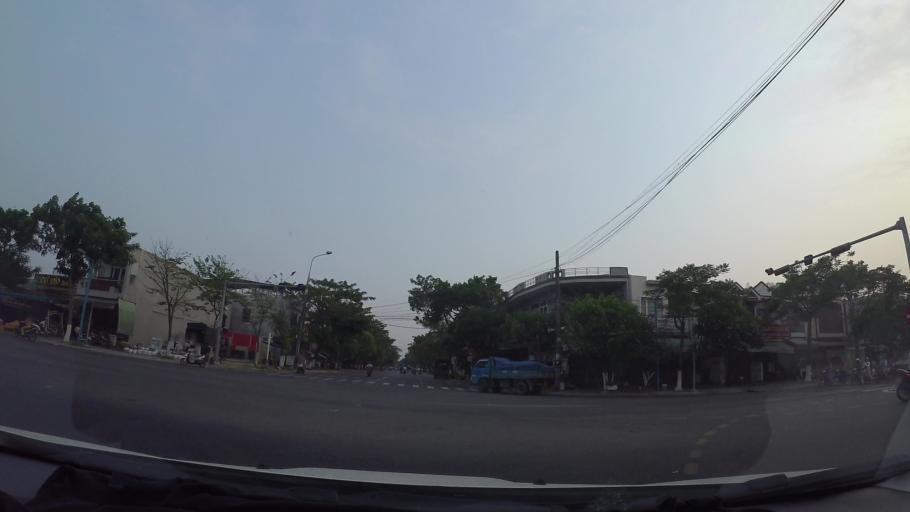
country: VN
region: Da Nang
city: Cam Le
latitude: 16.0228
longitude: 108.2021
